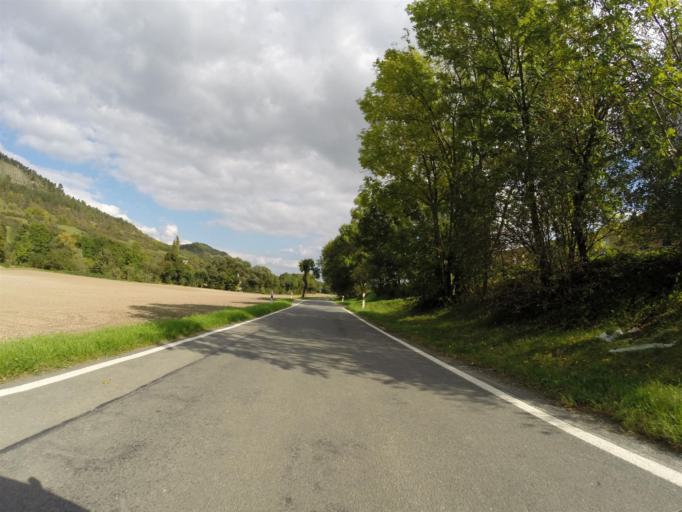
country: DE
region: Thuringia
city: Rothenstein
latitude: 50.8690
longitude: 11.5707
